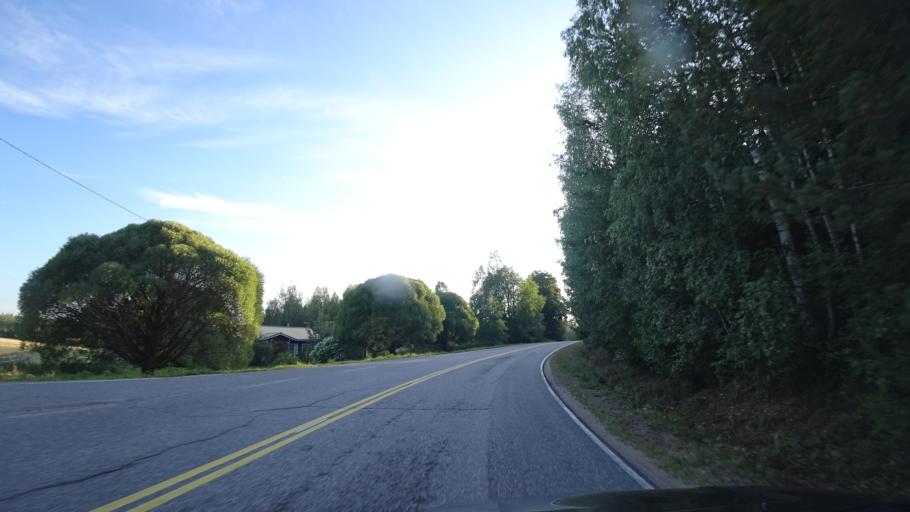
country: FI
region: Haeme
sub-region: Haemeenlinna
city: Lammi
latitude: 61.0070
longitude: 24.8804
